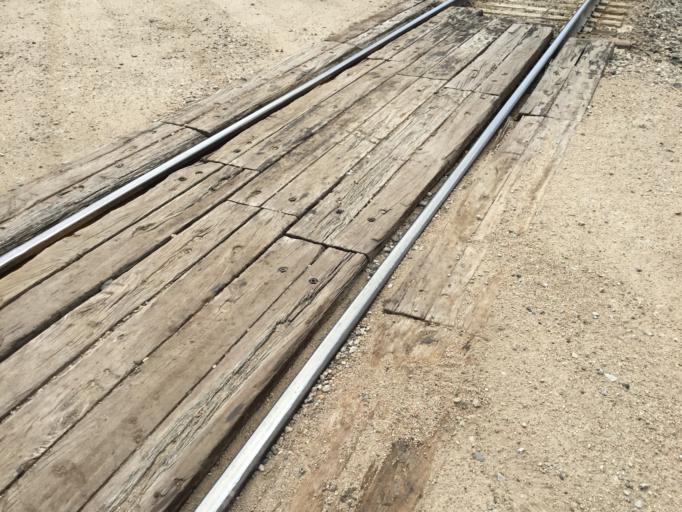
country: US
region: Kansas
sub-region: Cloud County
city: Concordia
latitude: 39.6827
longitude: -97.8404
